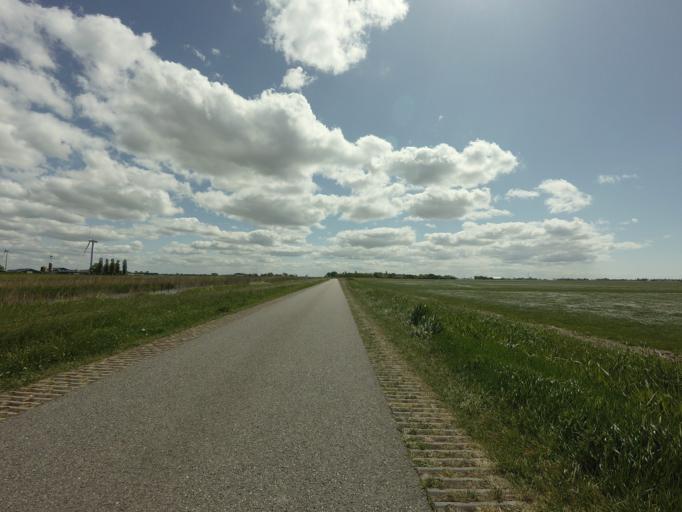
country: NL
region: Friesland
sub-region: Sudwest Fryslan
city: Makkum
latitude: 53.0909
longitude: 5.4152
